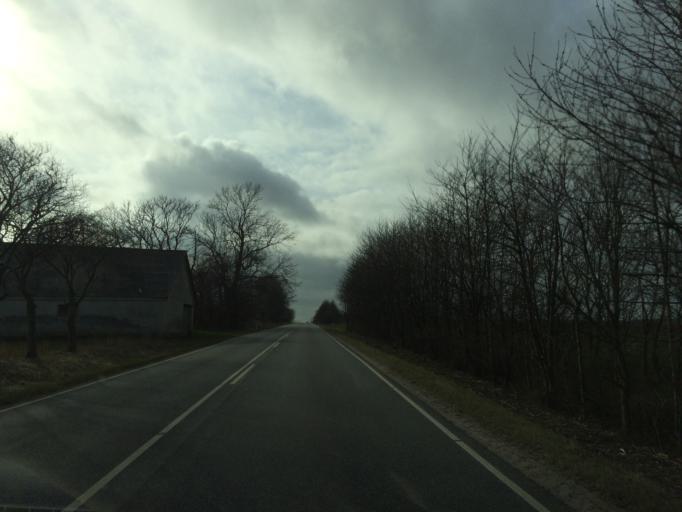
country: DK
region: Central Jutland
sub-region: Favrskov Kommune
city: Ulstrup
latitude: 56.4955
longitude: 9.8184
